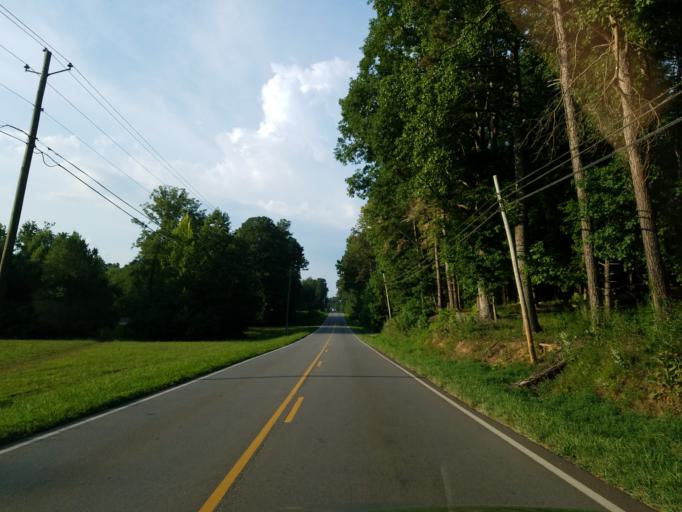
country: US
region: Georgia
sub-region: Gilmer County
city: Ellijay
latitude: 34.6425
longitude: -84.5071
